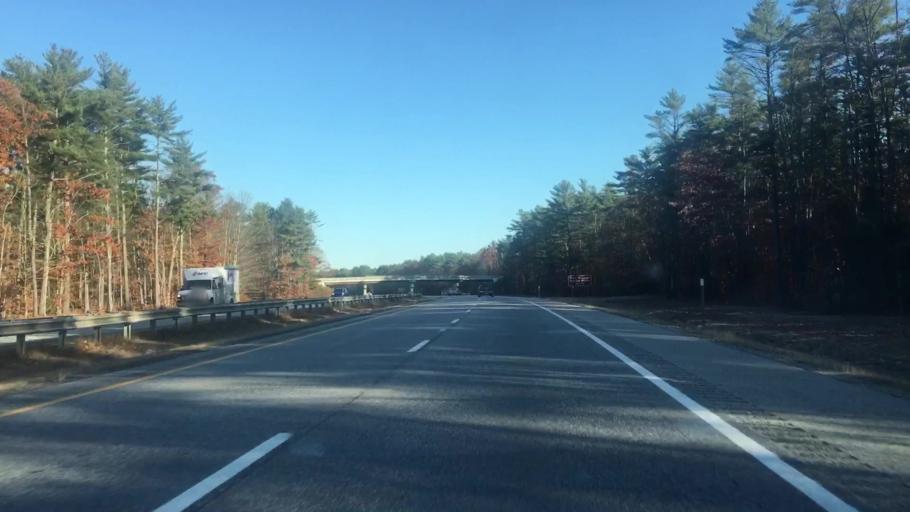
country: US
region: Maine
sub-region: Cumberland County
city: New Gloucester
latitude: 43.9827
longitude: -70.3108
